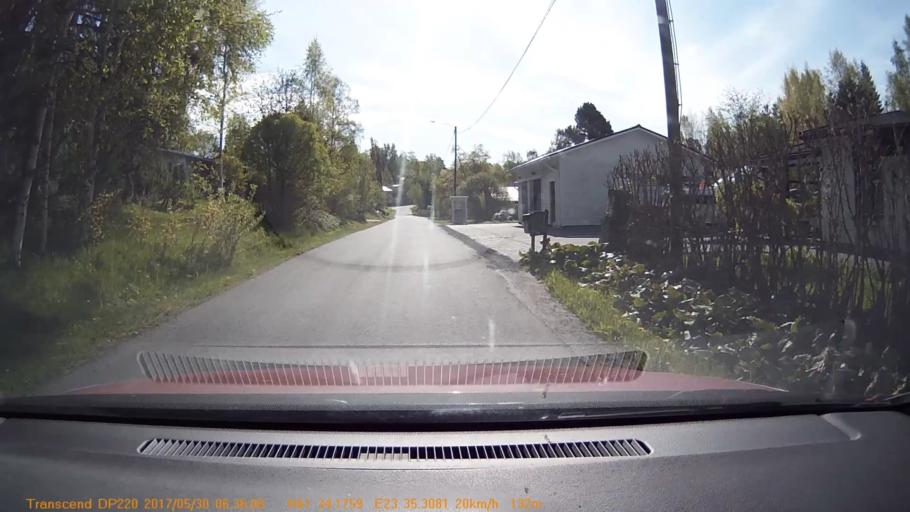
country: FI
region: Pirkanmaa
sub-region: Tampere
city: Yloejaervi
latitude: 61.5696
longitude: 23.5881
